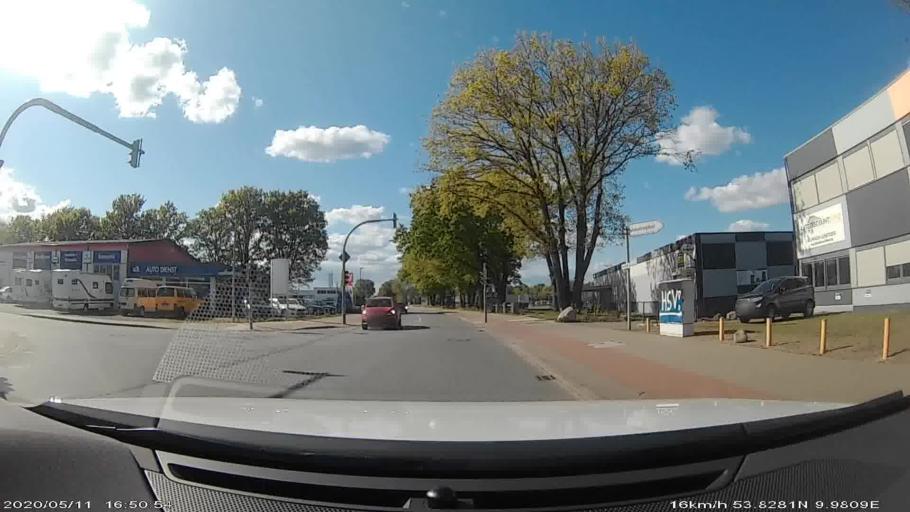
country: DE
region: Schleswig-Holstein
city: Oersdorf
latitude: 53.8320
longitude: 9.9726
